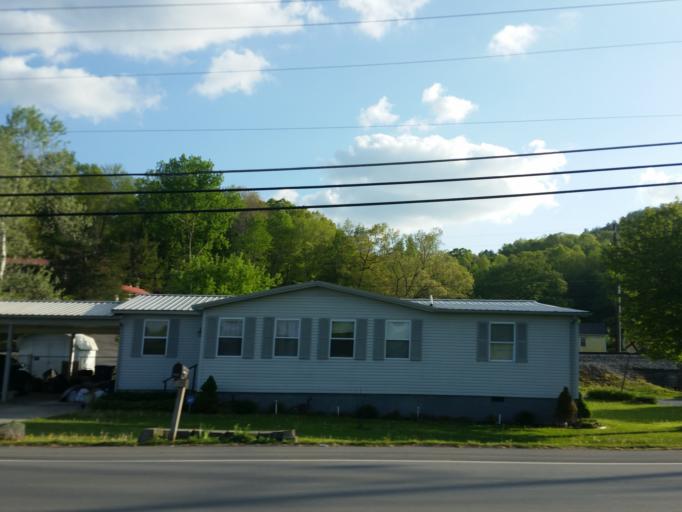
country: US
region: Kentucky
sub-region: Bell County
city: Middlesboro
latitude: 36.6091
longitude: -83.7522
